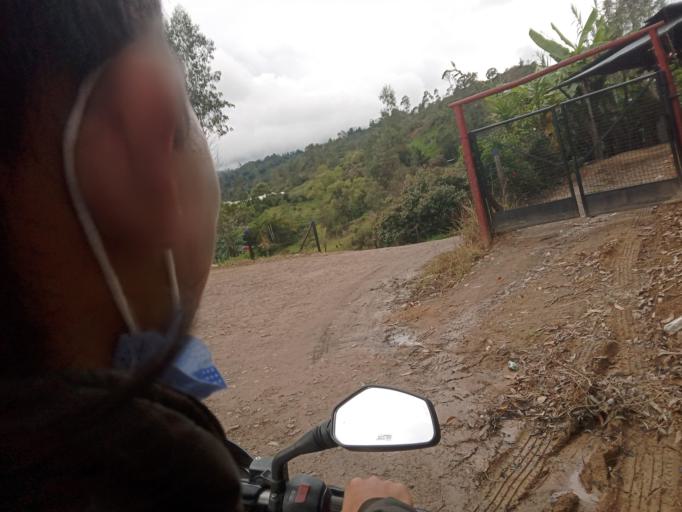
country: CO
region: Cundinamarca
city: Tenza
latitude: 5.1009
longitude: -73.4186
